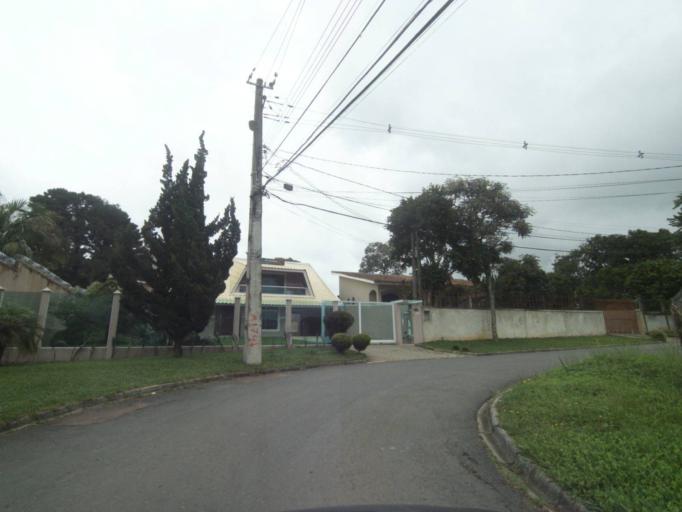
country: BR
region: Parana
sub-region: Curitiba
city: Curitiba
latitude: -25.4523
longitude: -49.3347
